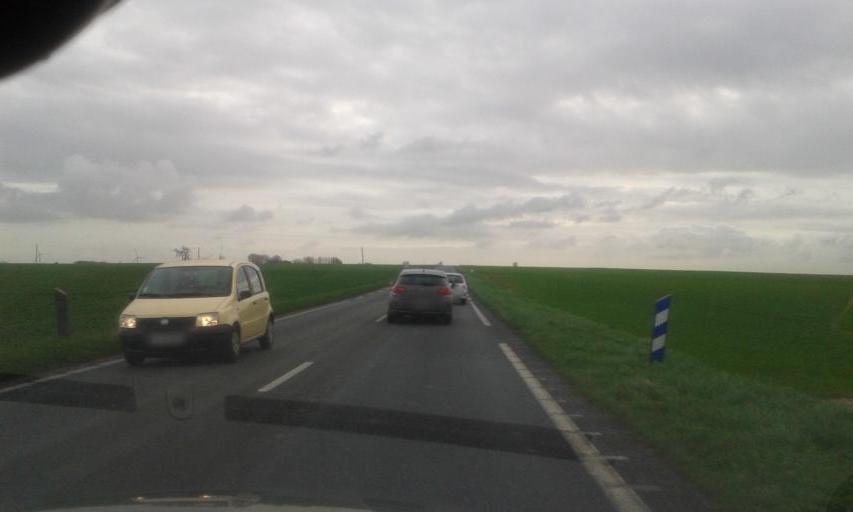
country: FR
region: Haute-Normandie
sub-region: Departement de la Seine-Maritime
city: Montmain
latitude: 49.3864
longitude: 1.2345
